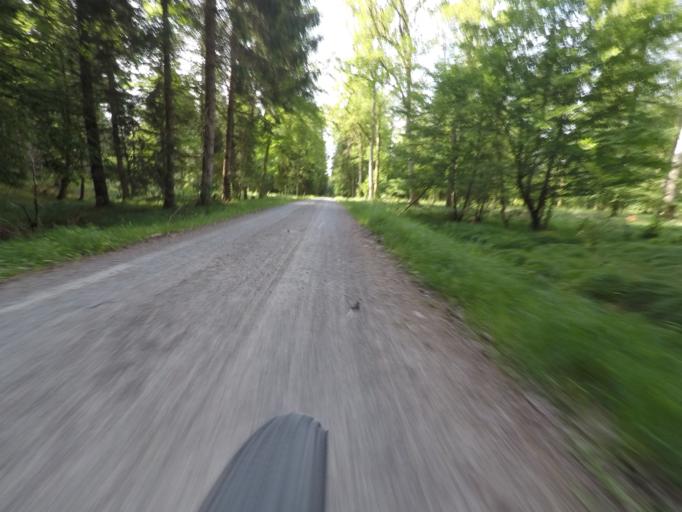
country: DE
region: Baden-Wuerttemberg
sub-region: Regierungsbezirk Stuttgart
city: Weil im Schonbuch
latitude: 48.5814
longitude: 9.0587
